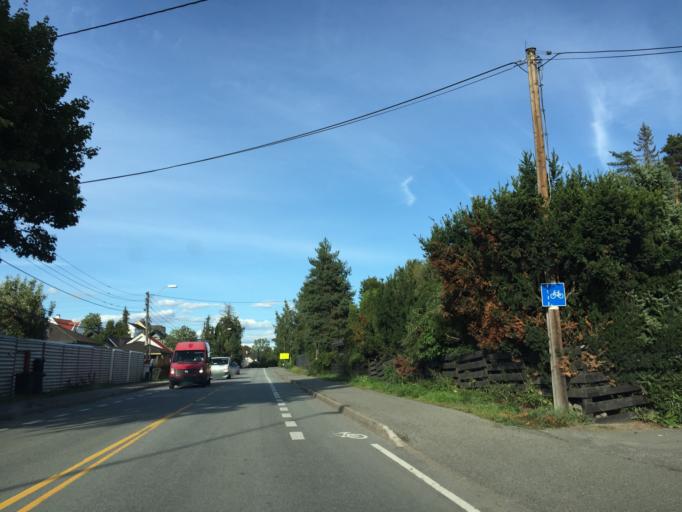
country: NO
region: Akershus
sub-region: Baerum
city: Lysaker
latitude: 59.9040
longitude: 10.5972
